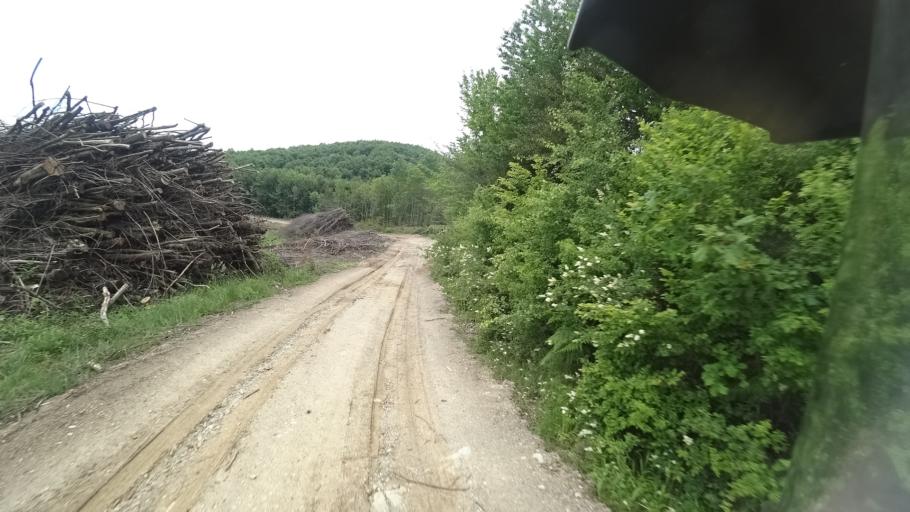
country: HR
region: Karlovacka
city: Vojnic
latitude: 45.2415
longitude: 15.6883
